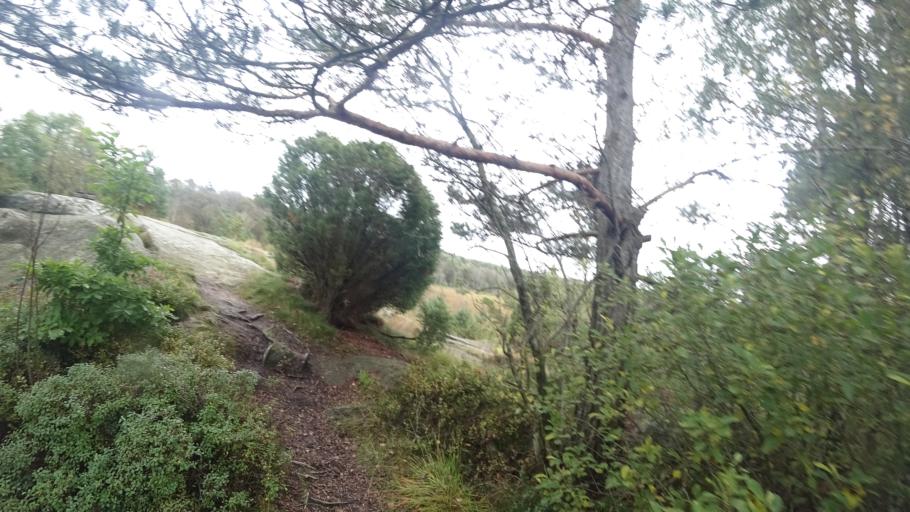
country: SE
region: Vaestra Goetaland
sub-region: Molndal
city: Moelndal
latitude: 57.6113
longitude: 11.9738
